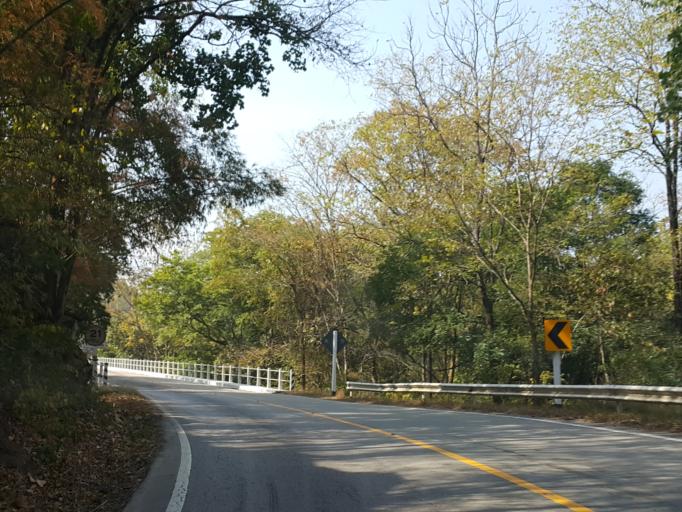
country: TH
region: Chiang Mai
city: Hot
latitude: 18.2264
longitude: 98.4937
